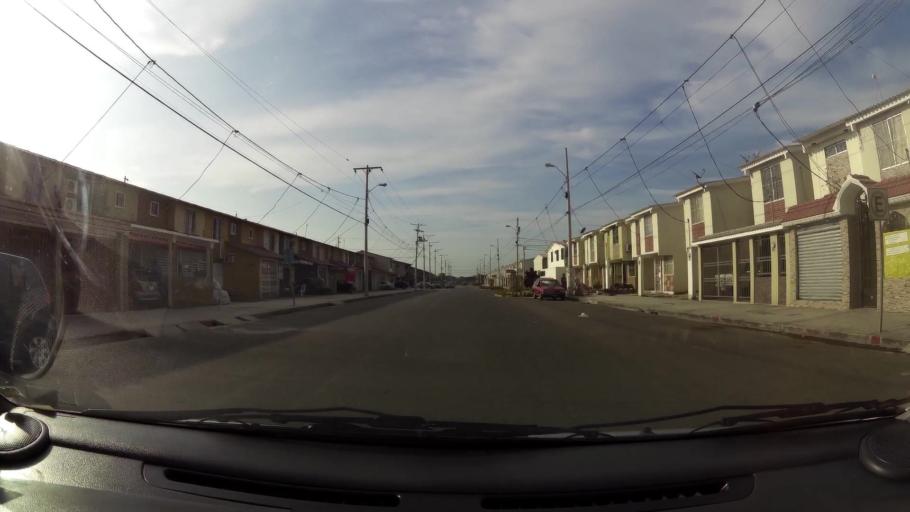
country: EC
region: Guayas
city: Eloy Alfaro
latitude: -2.0644
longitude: -79.8937
